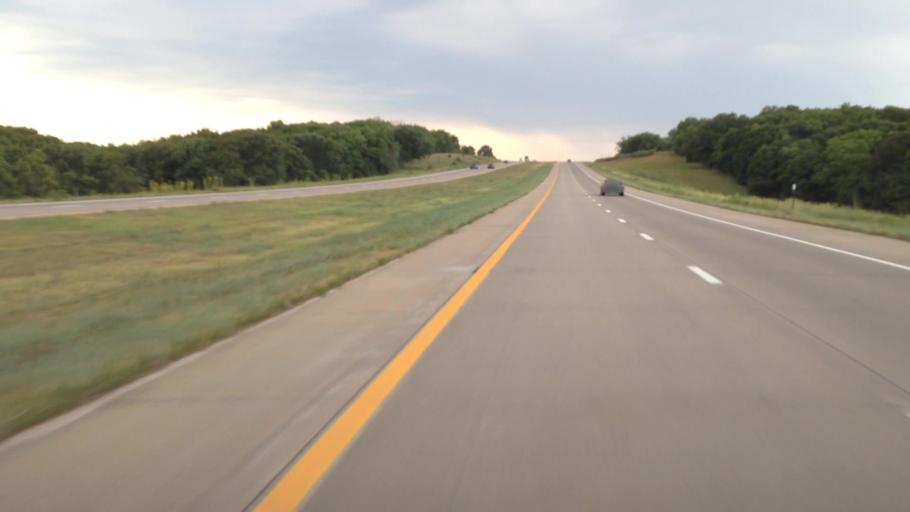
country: US
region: Kansas
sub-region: Osage County
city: Lyndon
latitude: 38.4807
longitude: -95.4999
